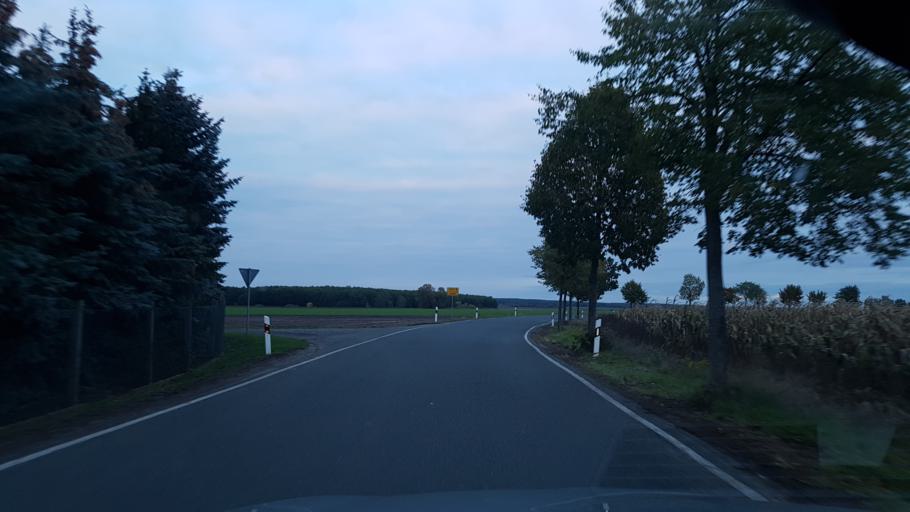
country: DE
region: Saxony
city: Grossenhain
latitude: 51.3263
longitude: 13.5601
